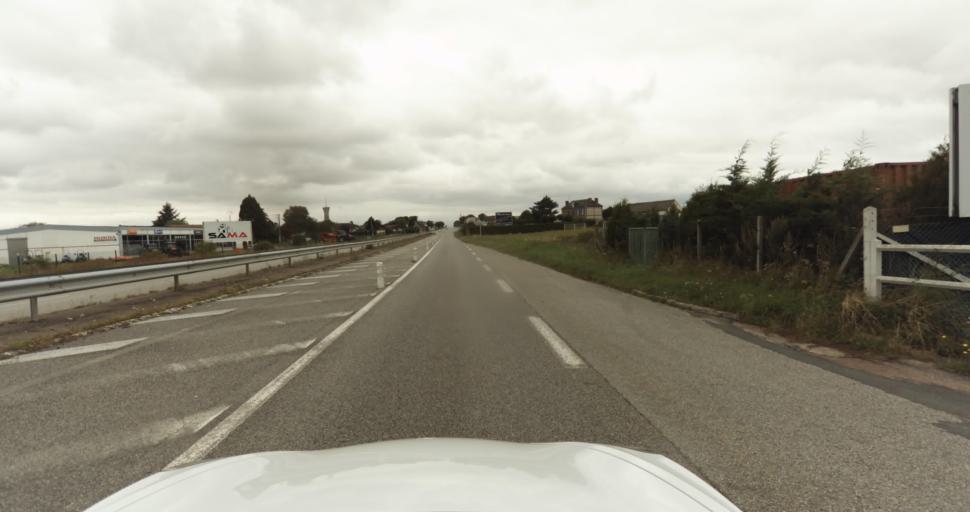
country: FR
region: Haute-Normandie
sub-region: Departement de l'Eure
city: Saint-Sebastien-de-Morsent
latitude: 49.0310
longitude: 1.1013
